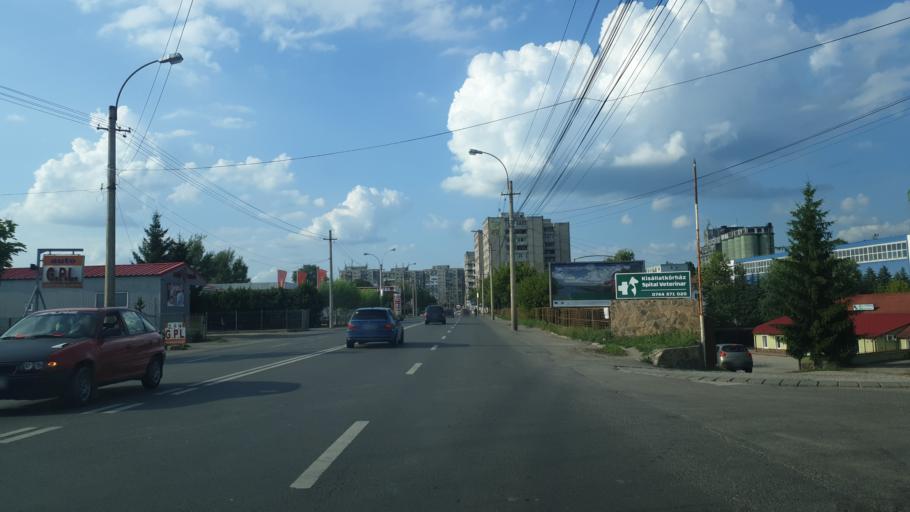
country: RO
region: Covasna
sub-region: Municipiul Sfantu Gheorghe
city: Sfantu-Gheorghe
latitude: 45.8585
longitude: 25.8074
